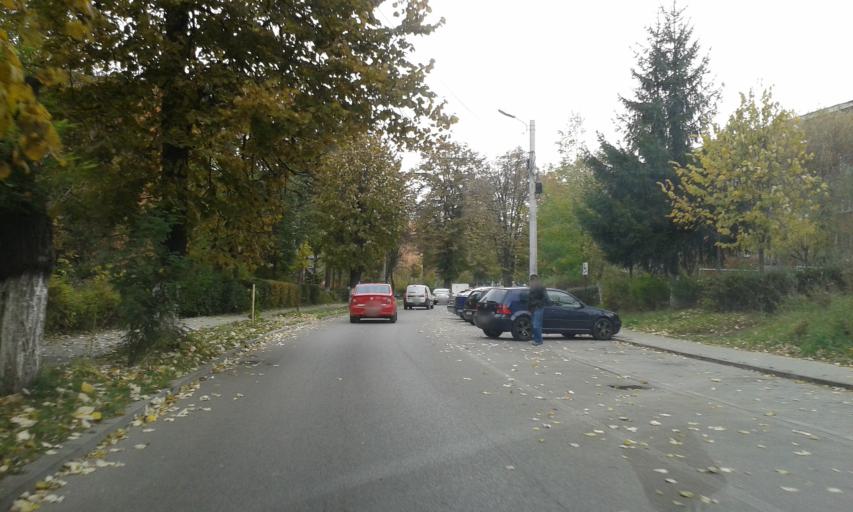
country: RO
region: Hunedoara
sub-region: Municipiul Petrosani
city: Petrosani
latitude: 45.3994
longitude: 23.3767
